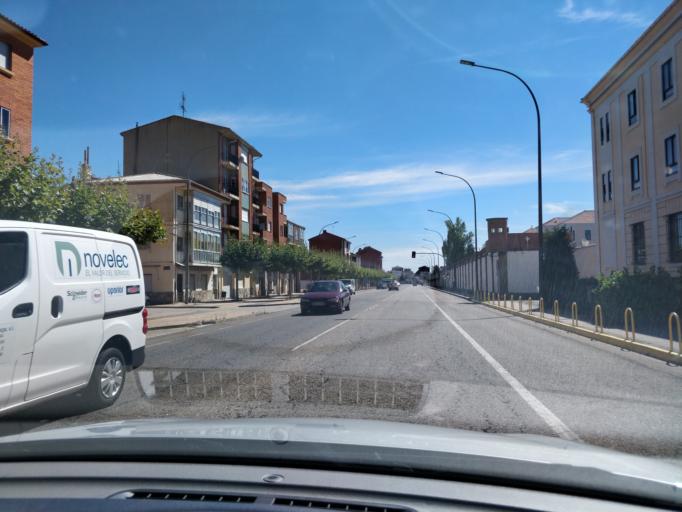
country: ES
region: Castille and Leon
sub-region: Provincia de Leon
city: Astorga
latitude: 42.4623
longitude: -6.0688
